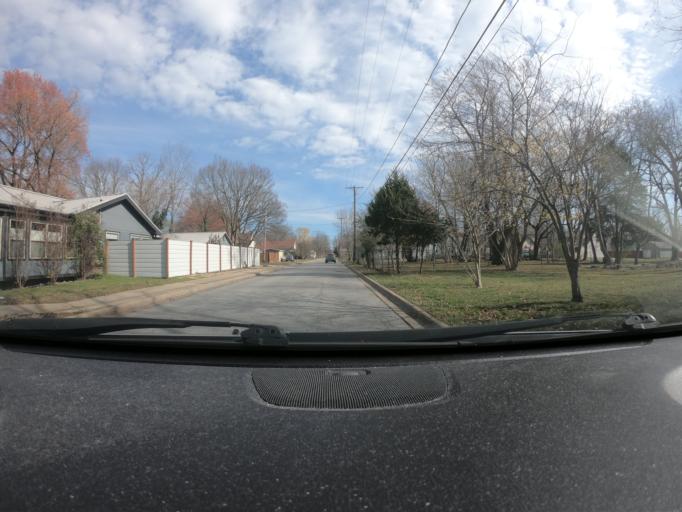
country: US
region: Arkansas
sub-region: Benton County
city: Rogers
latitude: 36.3372
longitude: -94.1225
